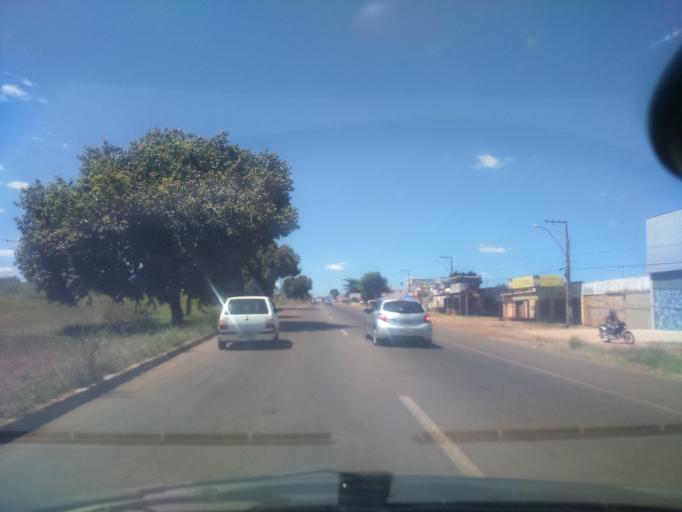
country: BR
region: Goias
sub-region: Luziania
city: Luziania
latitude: -16.0492
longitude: -48.0060
